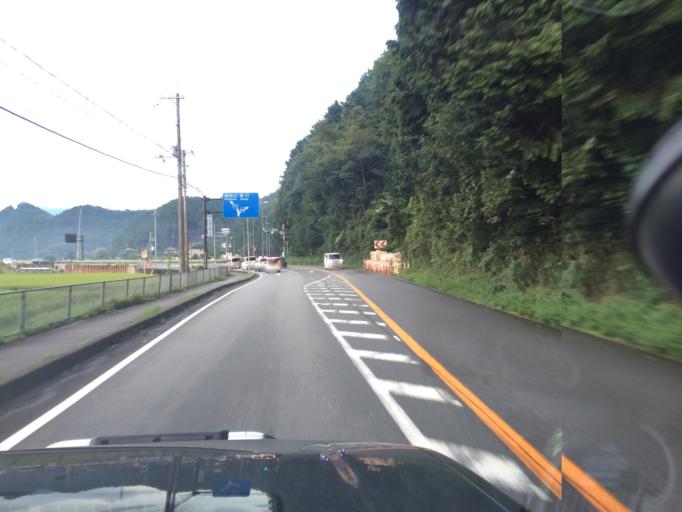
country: JP
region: Hyogo
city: Nishiwaki
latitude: 35.1350
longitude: 135.0227
